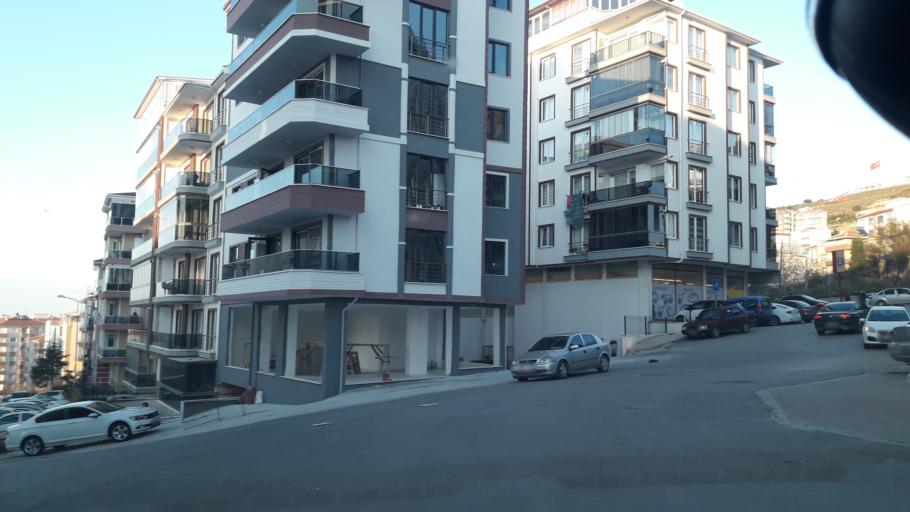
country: TR
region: Sinop
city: Sinop
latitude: 42.0249
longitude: 35.1607
